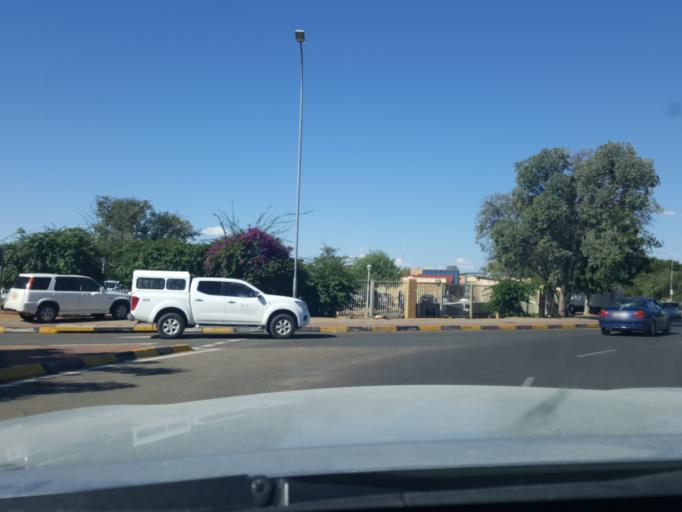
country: BW
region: South East
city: Gaborone
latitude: -24.6580
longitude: 25.9229
